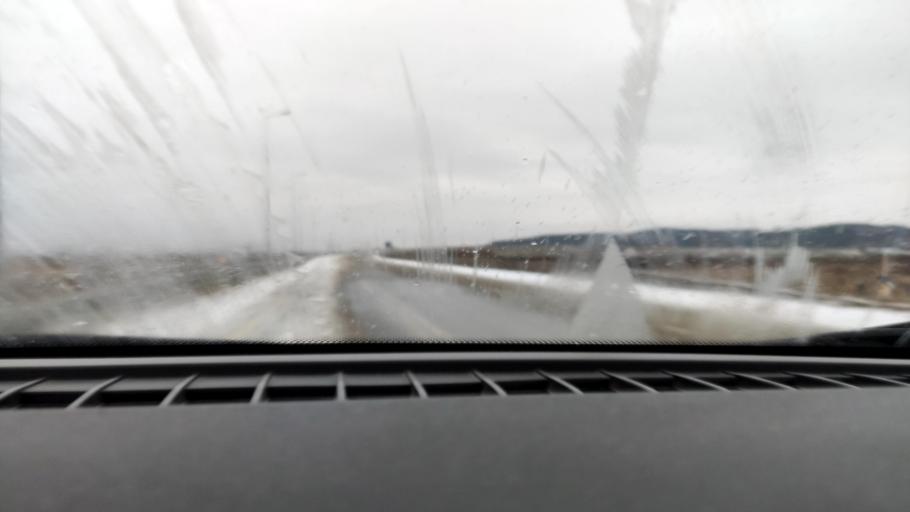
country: RU
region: Perm
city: Kondratovo
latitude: 57.9247
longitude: 56.1751
